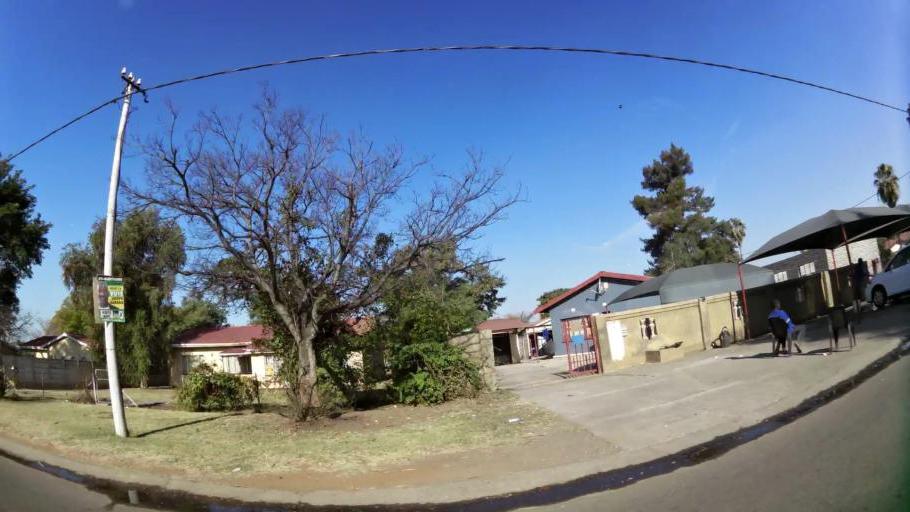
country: ZA
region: North-West
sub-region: Bojanala Platinum District Municipality
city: Rustenburg
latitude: -25.6525
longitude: 27.2392
